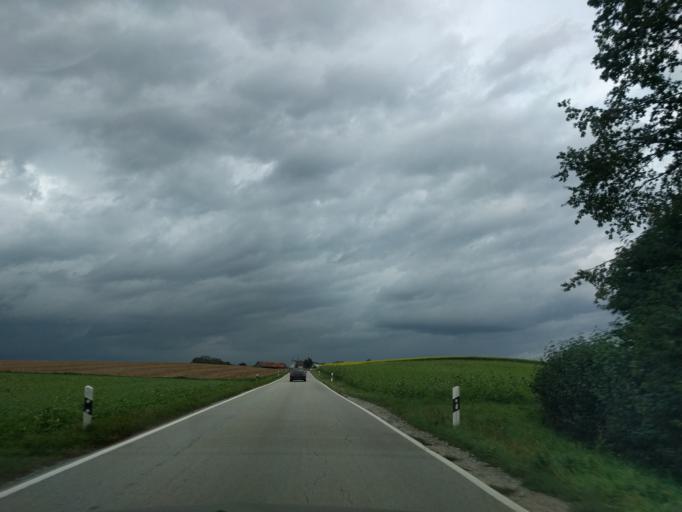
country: DE
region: Bavaria
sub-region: Lower Bavaria
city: Winzer
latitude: 48.7383
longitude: 13.0993
